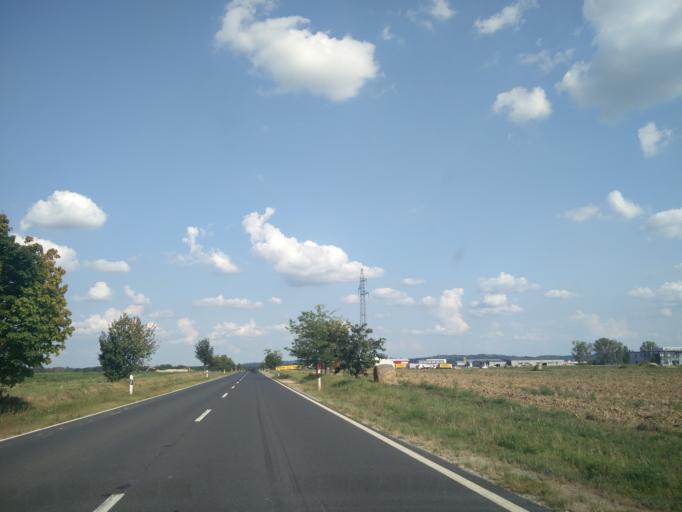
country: HU
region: Zala
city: Zalaegerszeg
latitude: 46.8813
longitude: 16.8314
